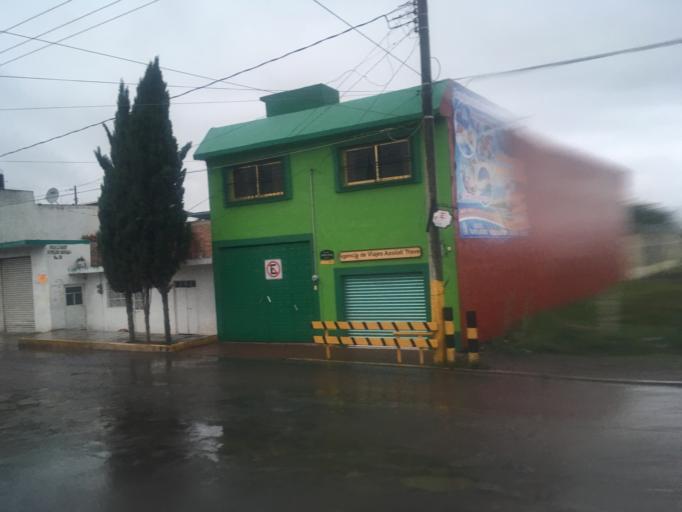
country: MX
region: Puebla
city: Chignahuapan
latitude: 19.8450
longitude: -98.0297
